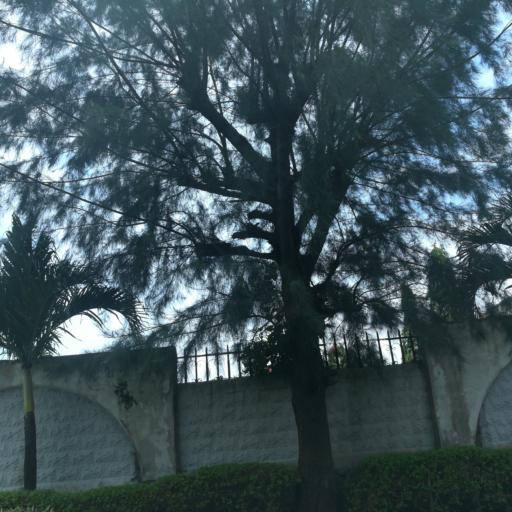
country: NG
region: Lagos
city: Ikoyi
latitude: 6.4388
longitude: 3.4660
